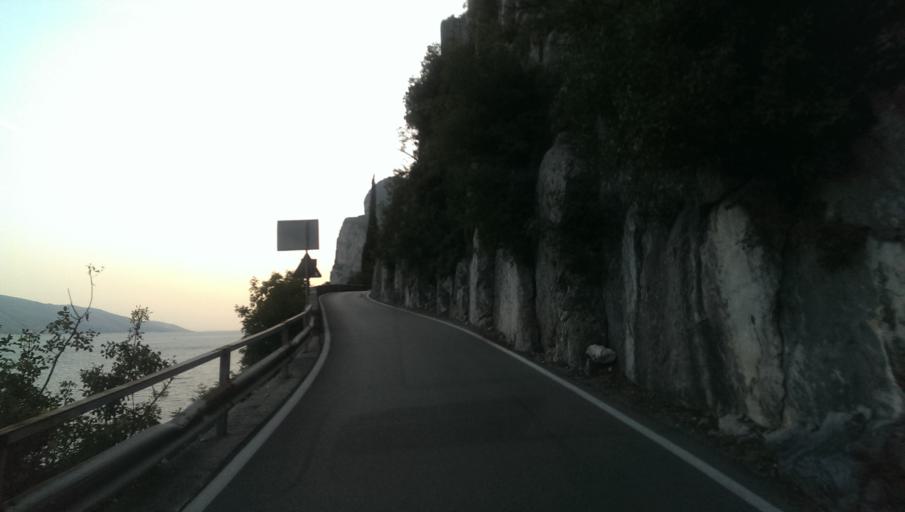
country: IT
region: Lombardy
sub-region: Provincia di Brescia
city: Pieve
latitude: 45.7677
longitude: 10.7610
